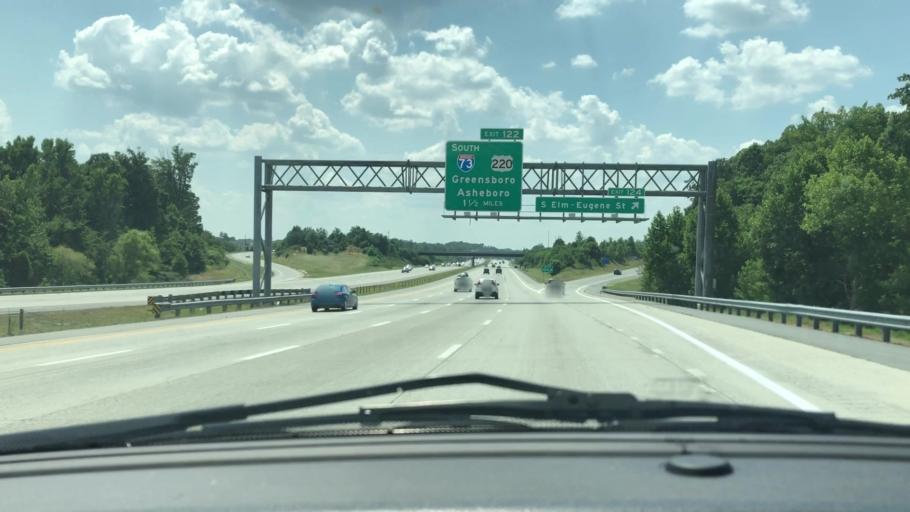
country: US
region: North Carolina
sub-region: Guilford County
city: Pleasant Garden
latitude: 36.0013
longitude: -79.7864
